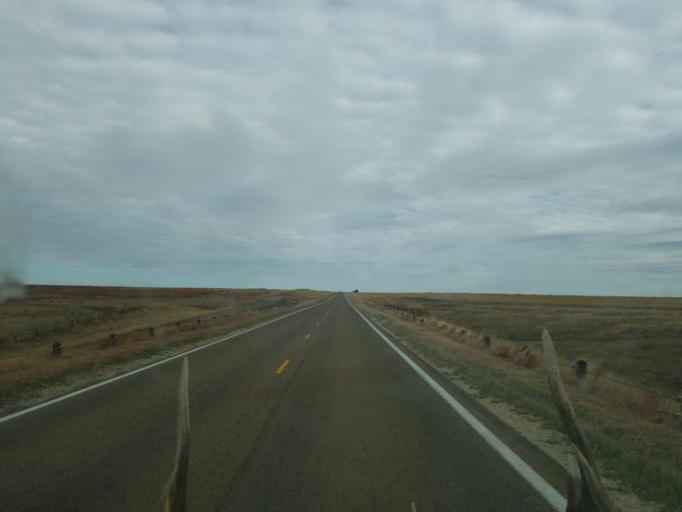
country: US
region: Kansas
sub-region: Wallace County
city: Sharon Springs
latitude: 39.0227
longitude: -101.3332
